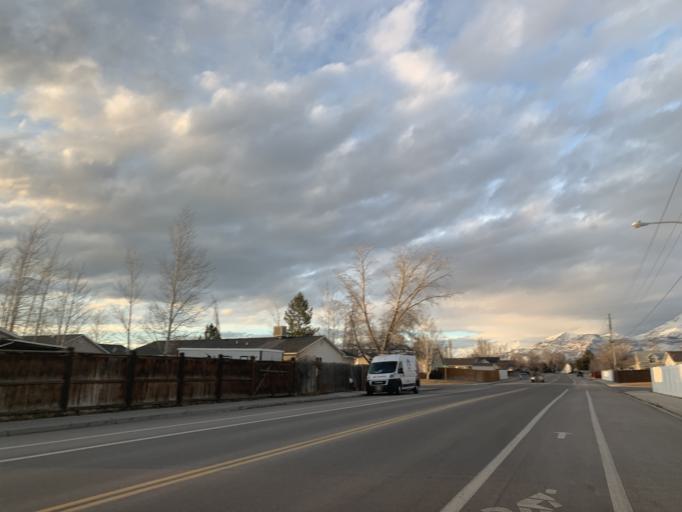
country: US
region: Utah
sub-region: Utah County
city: Provo
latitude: 40.2449
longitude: -111.7117
